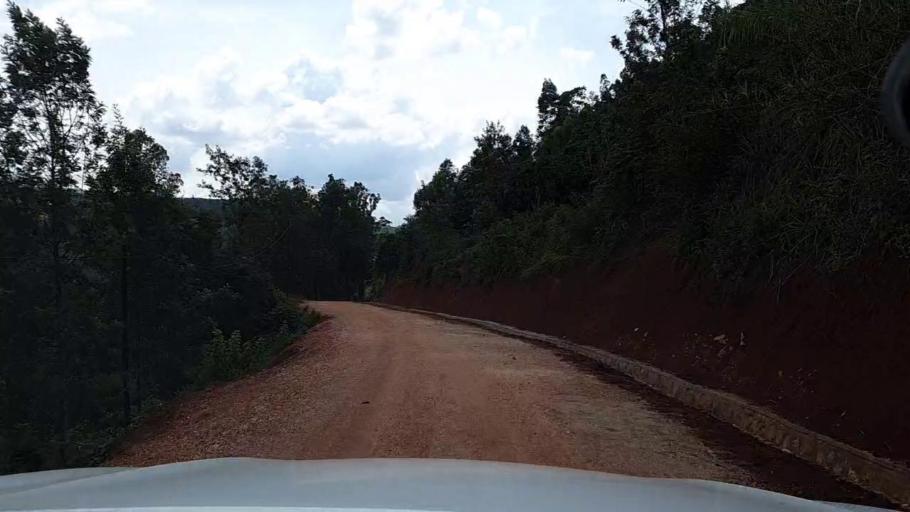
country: BI
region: Ngozi
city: Ngozi
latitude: -2.8103
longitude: 29.7316
